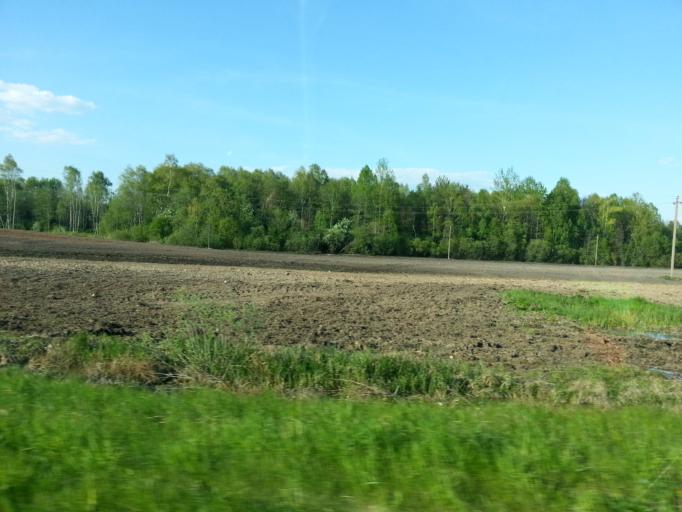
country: LT
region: Vilnius County
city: Ukmerge
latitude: 55.4014
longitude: 24.6893
